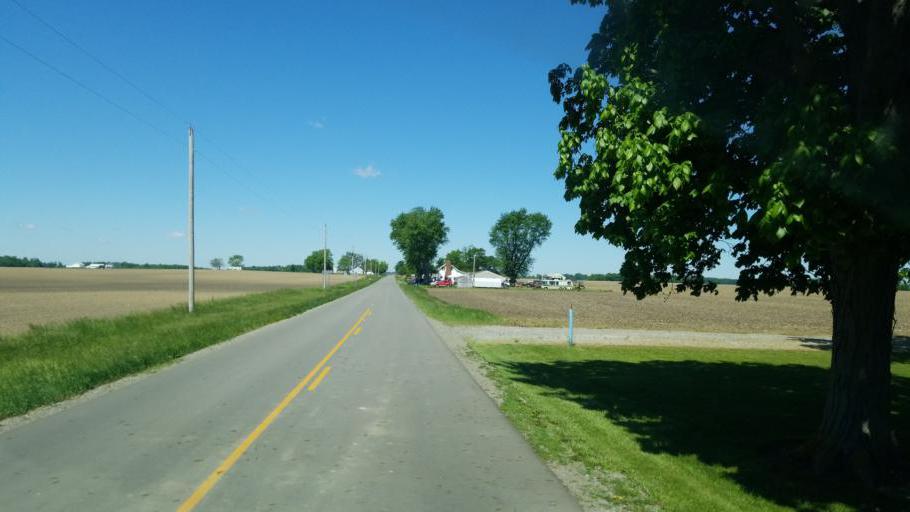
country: US
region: Ohio
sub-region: Logan County
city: Lakeview
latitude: 40.4174
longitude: -83.9467
